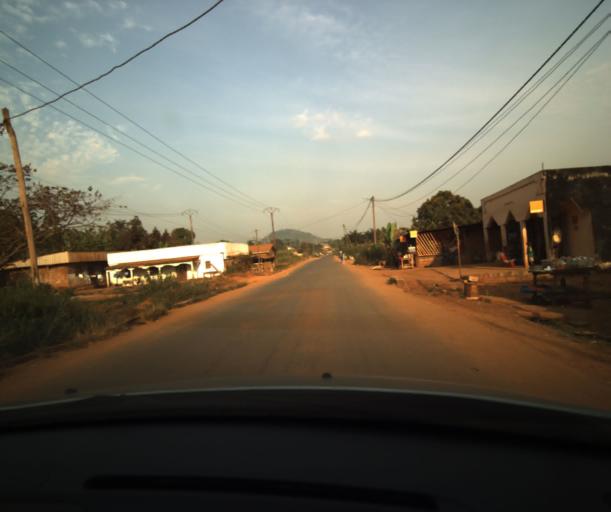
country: CM
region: Centre
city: Yaounde
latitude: 3.8741
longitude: 11.4429
